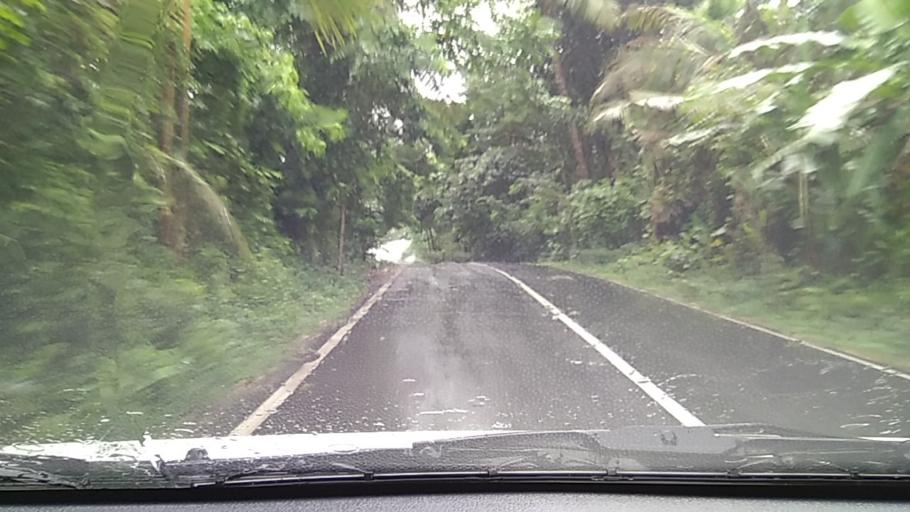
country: ID
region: Bali
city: Banjar Danginsema
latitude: -8.4723
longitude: 115.6192
